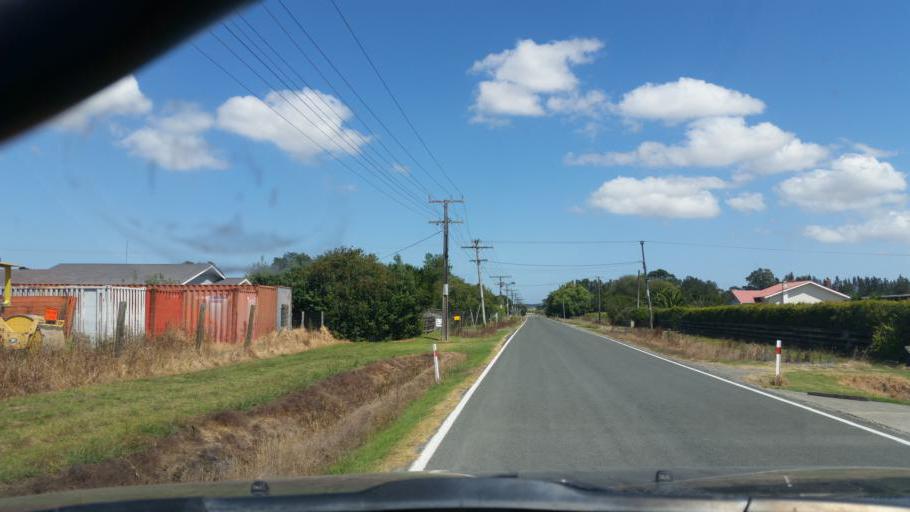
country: NZ
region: Northland
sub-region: Kaipara District
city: Dargaville
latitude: -35.9443
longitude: 173.8591
